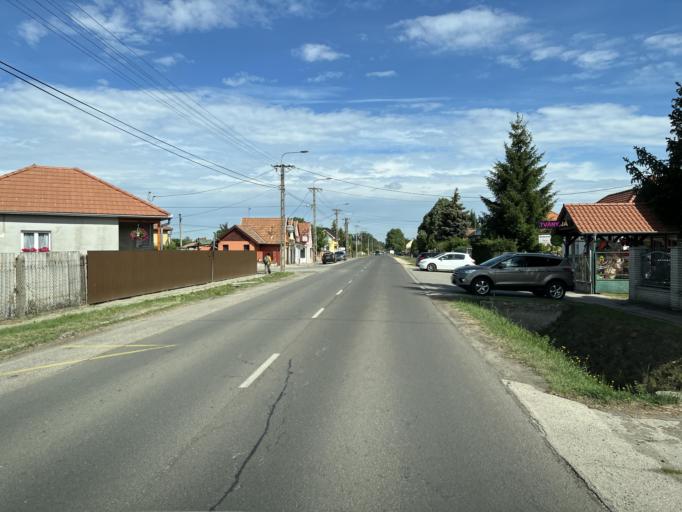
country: HU
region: Pest
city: Isaszeg
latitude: 47.5436
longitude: 19.3909
